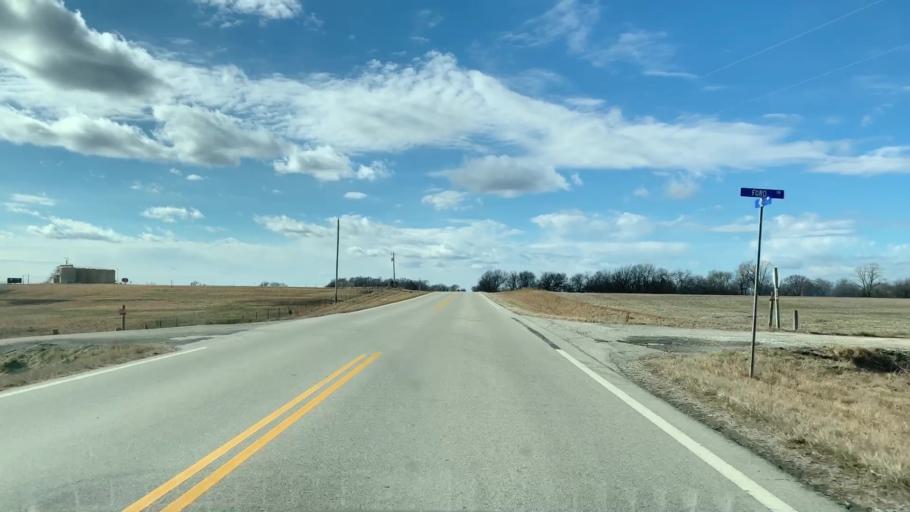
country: US
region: Kansas
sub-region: Neosho County
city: Chanute
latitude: 37.5288
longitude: -95.4341
